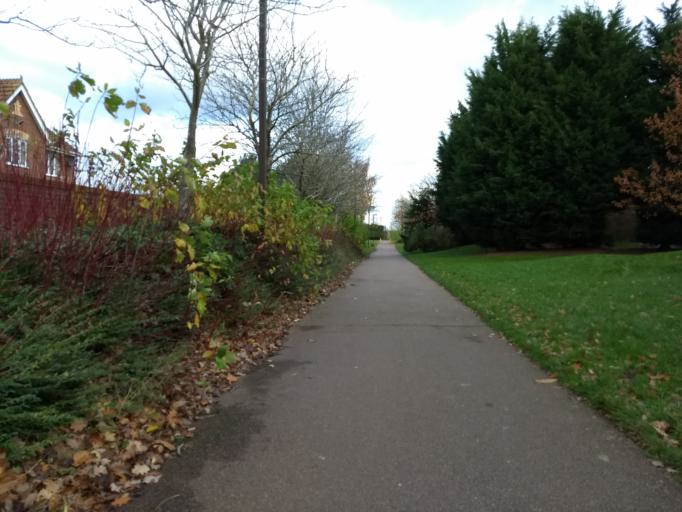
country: GB
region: England
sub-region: Milton Keynes
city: Shenley Church End
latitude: 52.0061
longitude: -0.7769
